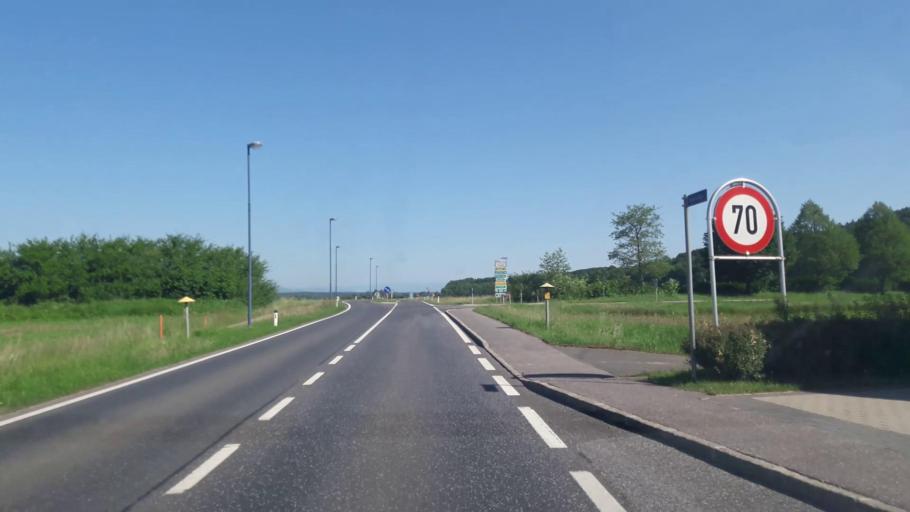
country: AT
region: Burgenland
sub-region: Politischer Bezirk Jennersdorf
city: Rudersdorf
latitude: 47.0590
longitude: 16.1172
